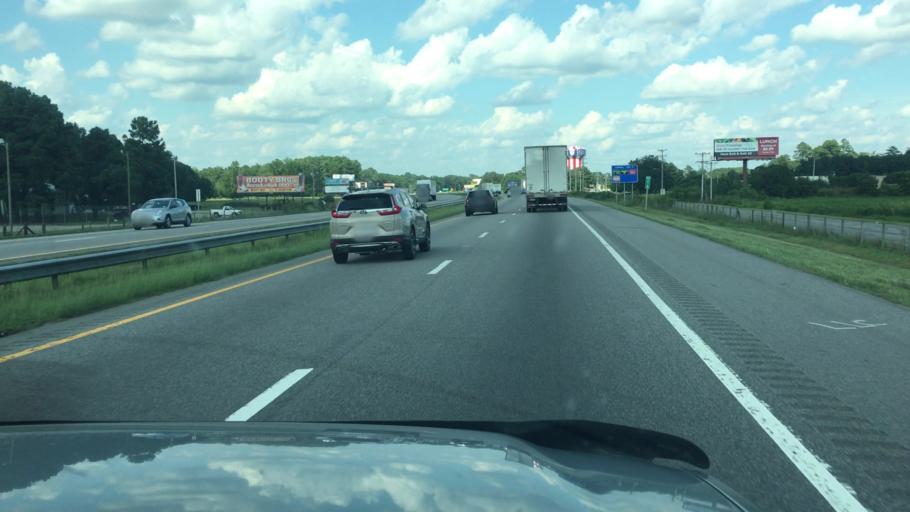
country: US
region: North Carolina
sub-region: Robeson County
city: Lumberton
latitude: 34.6157
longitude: -79.0686
